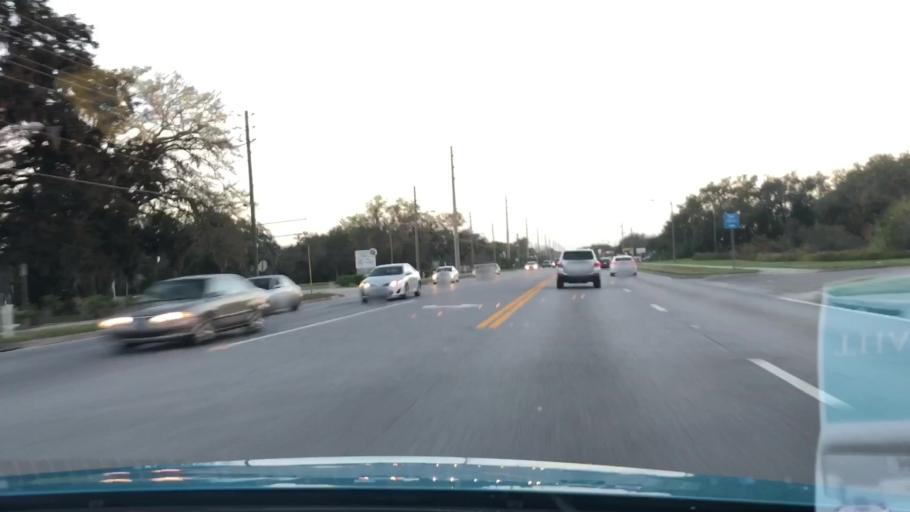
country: US
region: Florida
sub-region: Osceola County
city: Kissimmee
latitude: 28.3240
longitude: -81.3913
